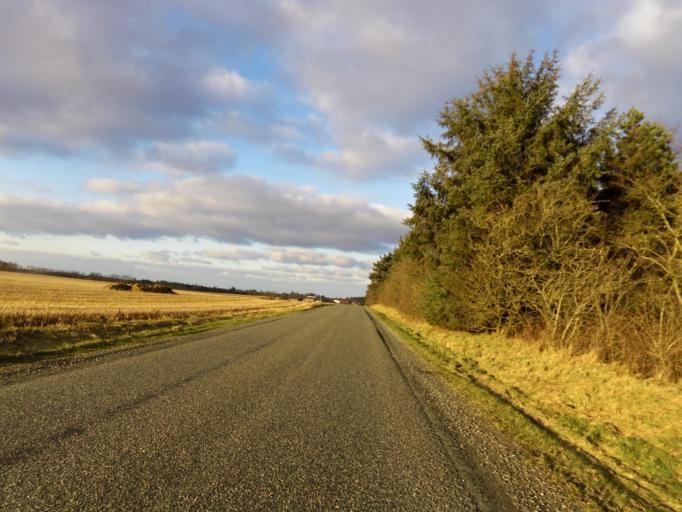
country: DK
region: South Denmark
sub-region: Esbjerg Kommune
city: Ribe
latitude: 55.2975
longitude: 8.8485
